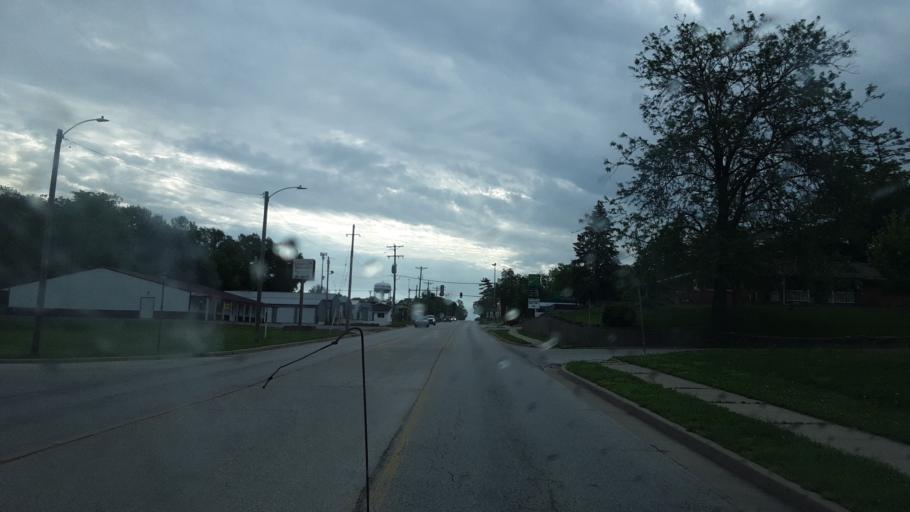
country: US
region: Illinois
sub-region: Hancock County
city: Hamilton
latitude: 40.3965
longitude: -91.3415
